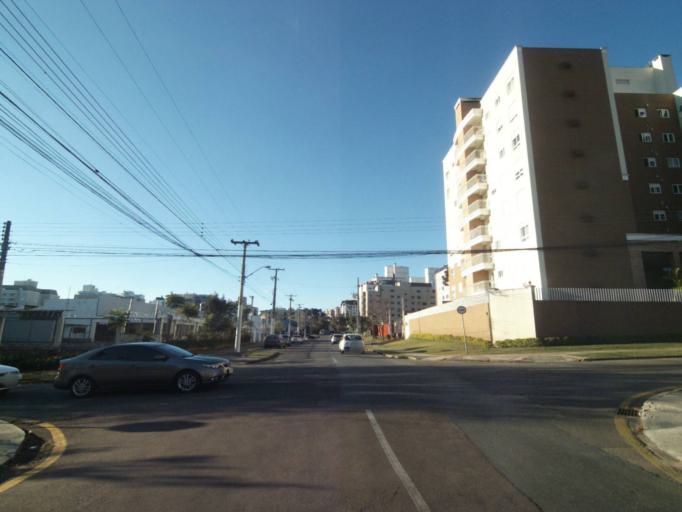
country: BR
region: Parana
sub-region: Curitiba
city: Curitiba
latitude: -25.4583
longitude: -49.2921
